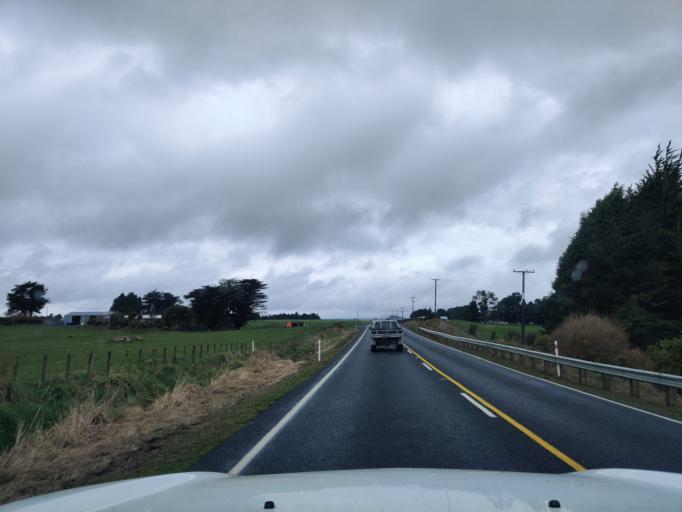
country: NZ
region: Manawatu-Wanganui
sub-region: Ruapehu District
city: Waiouru
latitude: -39.3619
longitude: 175.3449
